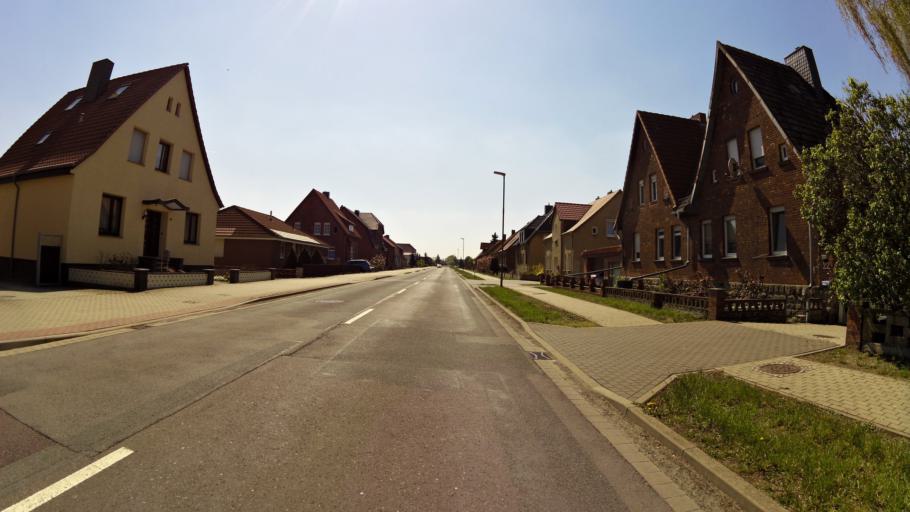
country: DE
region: Saxony-Anhalt
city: Oebisfelde
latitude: 52.4478
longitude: 10.9967
